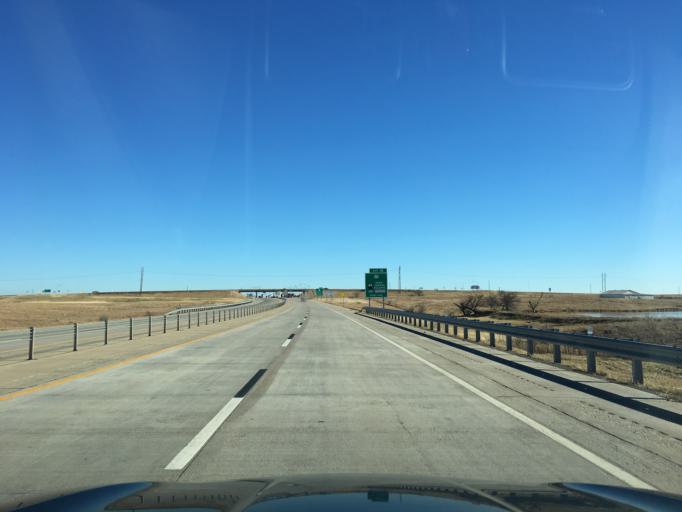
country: US
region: Oklahoma
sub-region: Noble County
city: Perry
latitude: 36.3838
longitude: -97.0745
